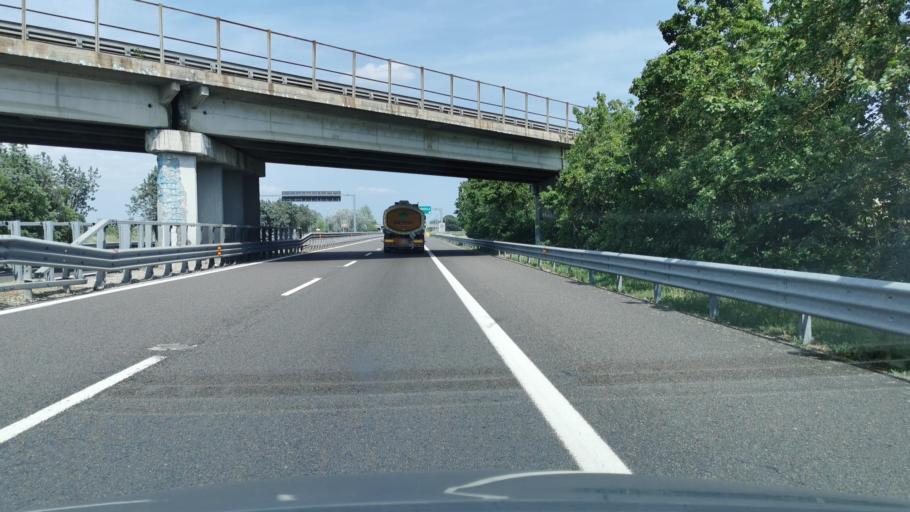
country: IT
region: Emilia-Romagna
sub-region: Provincia di Ravenna
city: Cotignola
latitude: 44.3890
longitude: 11.9172
